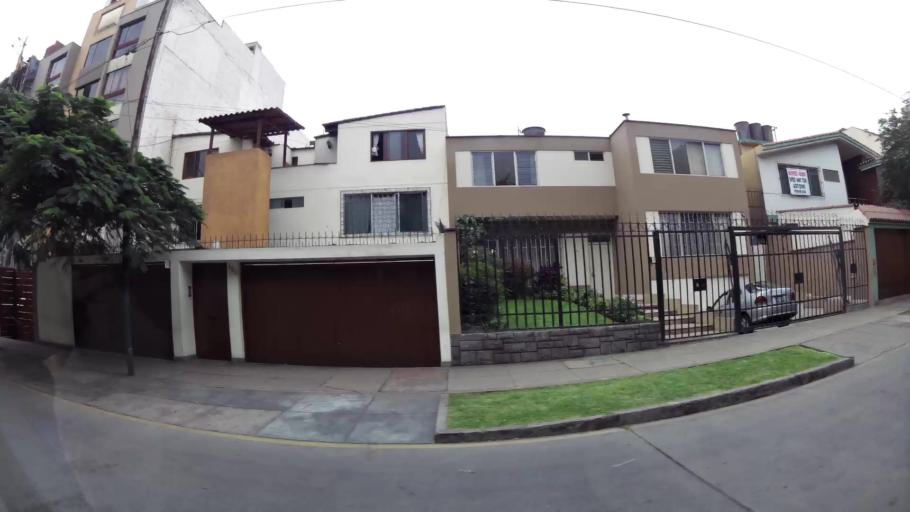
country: PE
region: Lima
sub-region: Lima
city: Surco
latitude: -12.1323
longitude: -77.0031
